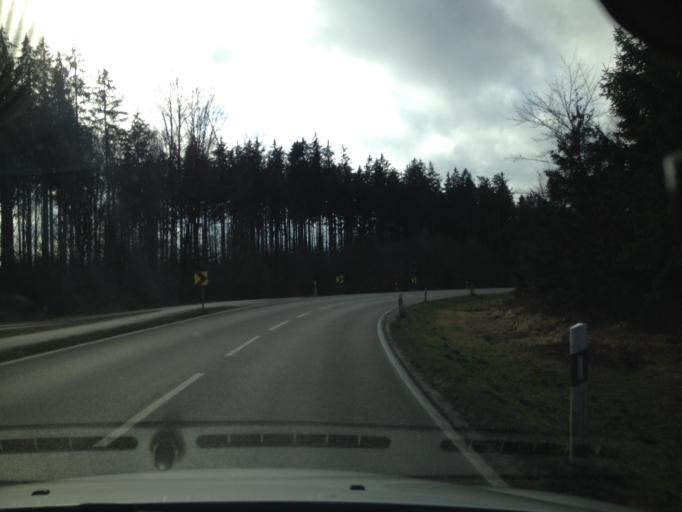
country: DE
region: Bavaria
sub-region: Swabia
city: Wehringen
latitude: 48.2630
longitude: 10.7747
